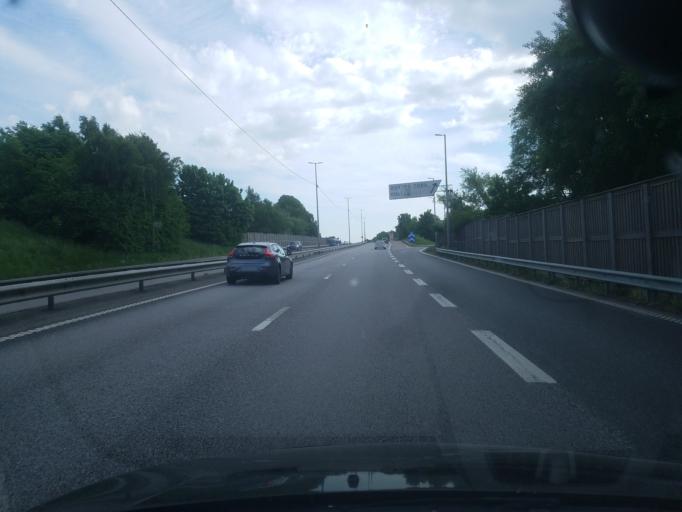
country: SE
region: Vaestra Goetaland
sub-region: Goteborg
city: Majorna
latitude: 57.6377
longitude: 11.9318
